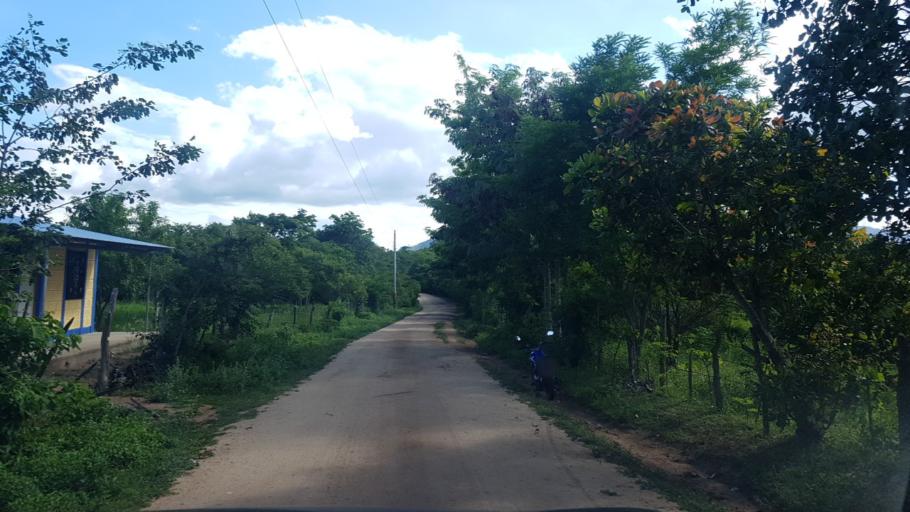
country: NI
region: Nueva Segovia
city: Mozonte
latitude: 13.6543
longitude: -86.3982
